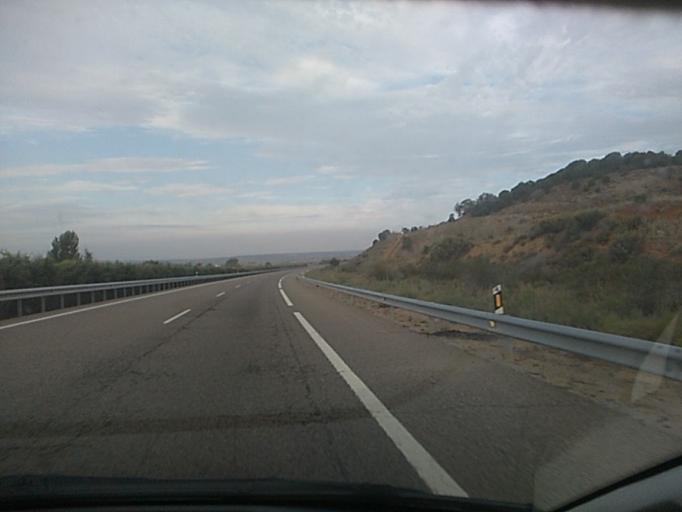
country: ES
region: Castille and Leon
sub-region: Provincia de Zamora
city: Quiruelas de Vidriales
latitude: 42.0265
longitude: -5.8050
